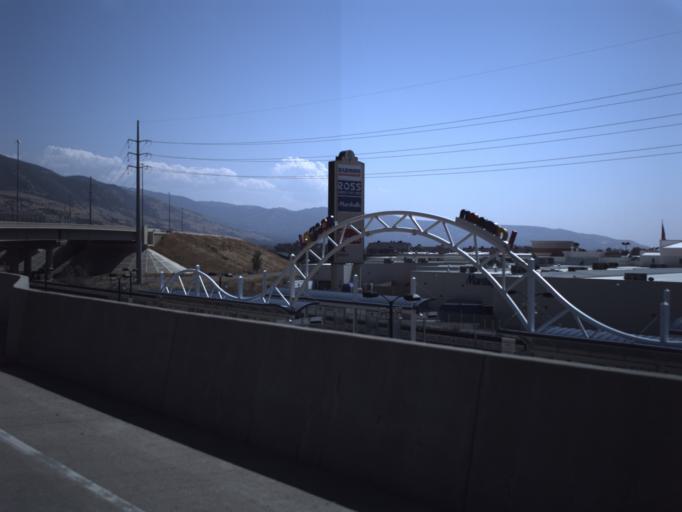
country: US
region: Utah
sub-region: Davis County
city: Farmington
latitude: 40.9877
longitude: -111.9038
